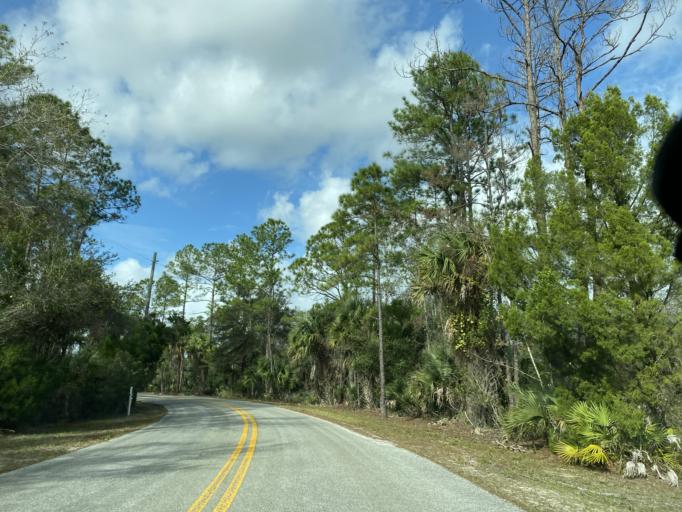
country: US
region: Florida
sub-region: Orange County
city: Christmas
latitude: 28.4547
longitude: -80.9779
